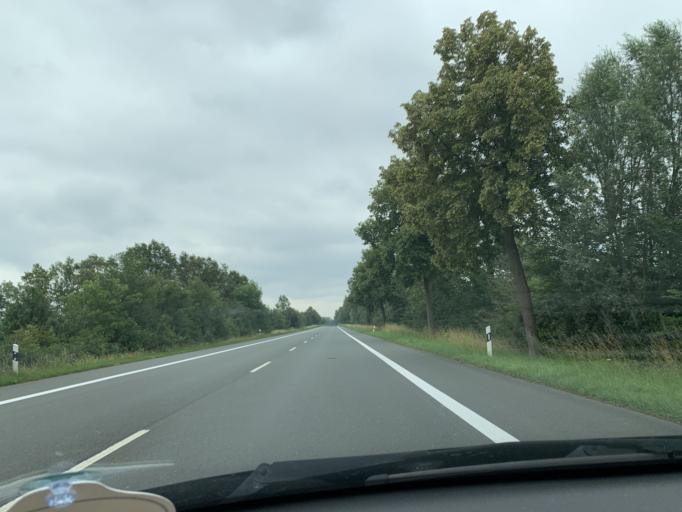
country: DE
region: North Rhine-Westphalia
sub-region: Regierungsbezirk Munster
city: Warendorf
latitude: 51.9128
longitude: 8.0438
